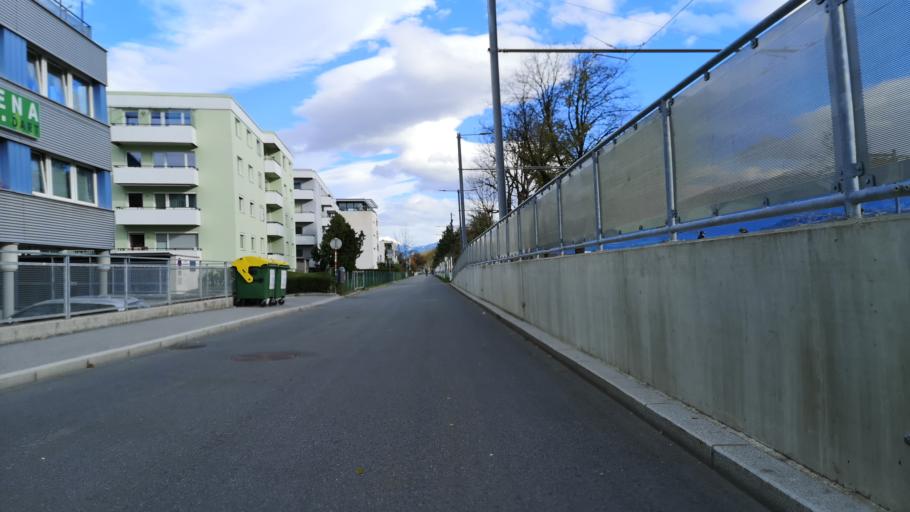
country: AT
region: Tyrol
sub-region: Politischer Bezirk Innsbruck Land
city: Vols
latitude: 47.2635
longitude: 11.3568
